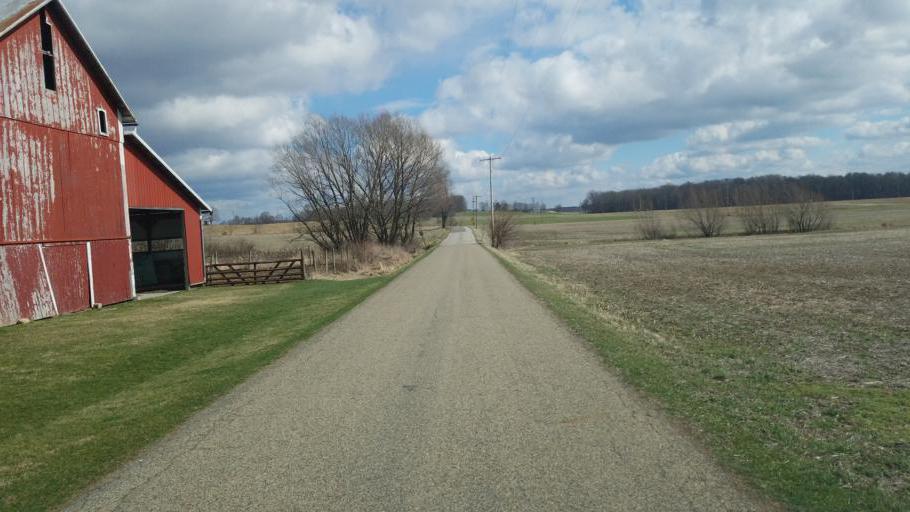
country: US
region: Ohio
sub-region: Knox County
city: Fredericktown
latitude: 40.5442
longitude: -82.5315
